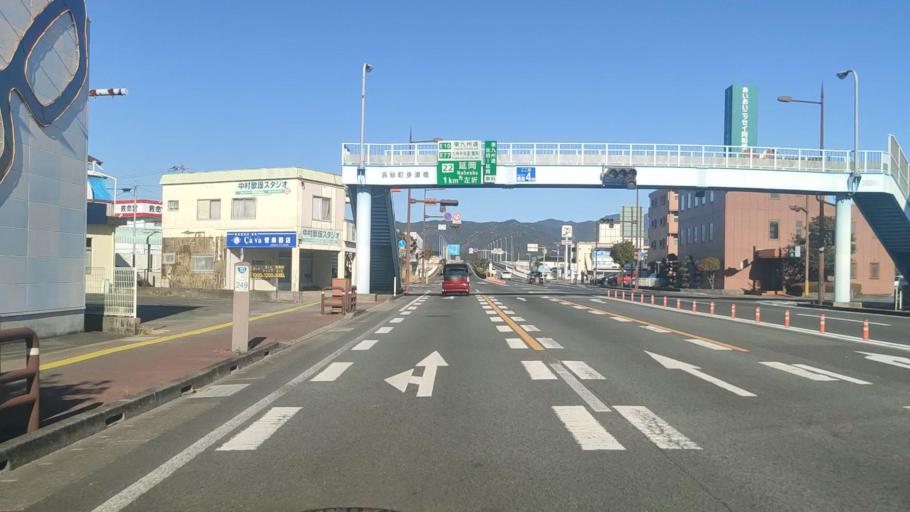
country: JP
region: Miyazaki
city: Nobeoka
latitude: 32.5790
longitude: 131.6828
